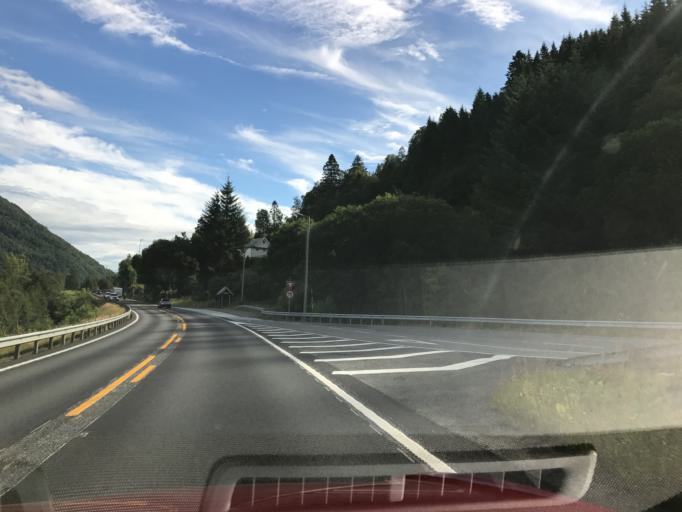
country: NO
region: Hordaland
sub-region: Bergen
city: Indre Arna
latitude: 60.4251
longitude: 5.5688
